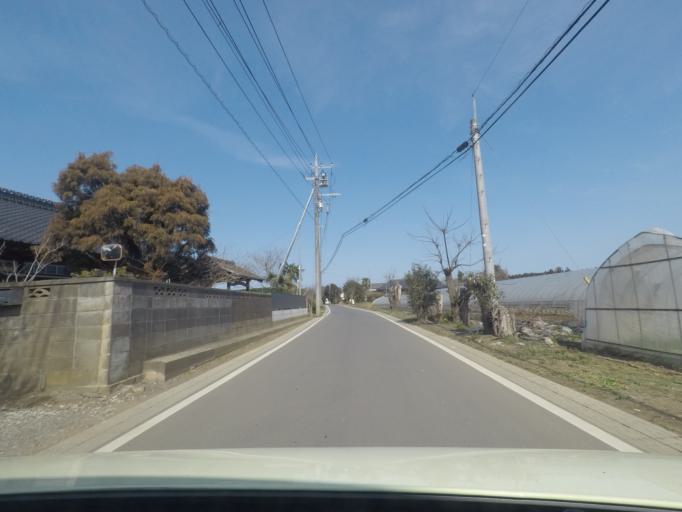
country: JP
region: Ibaraki
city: Okunoya
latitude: 36.2199
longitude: 140.4427
